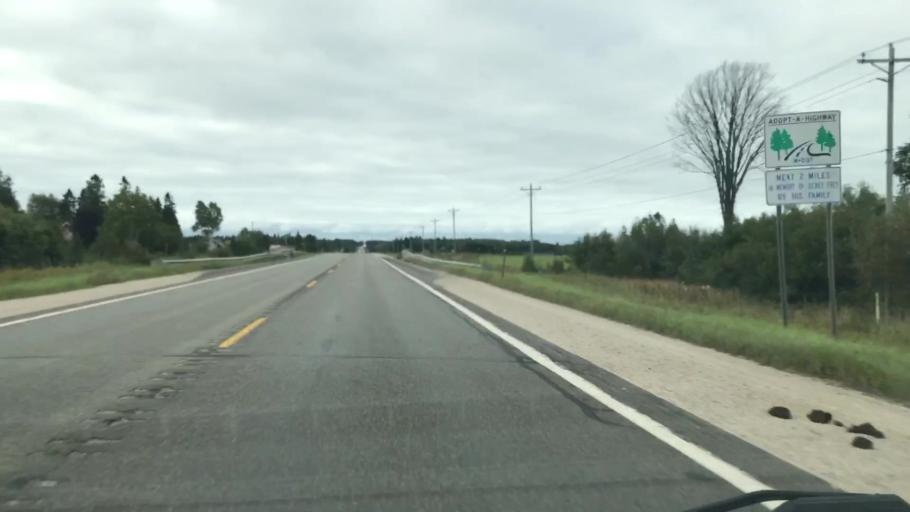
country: US
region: Michigan
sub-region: Luce County
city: Newberry
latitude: 46.1486
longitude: -85.5714
